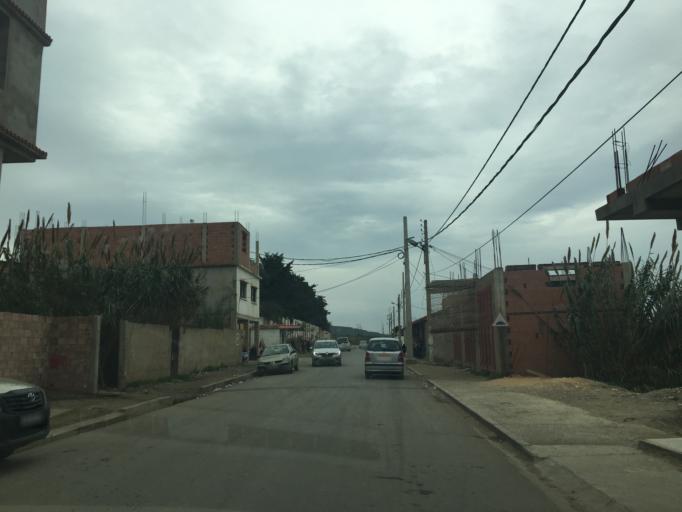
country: DZ
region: Tipaza
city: Tipasa
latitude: 36.6257
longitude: 2.2722
